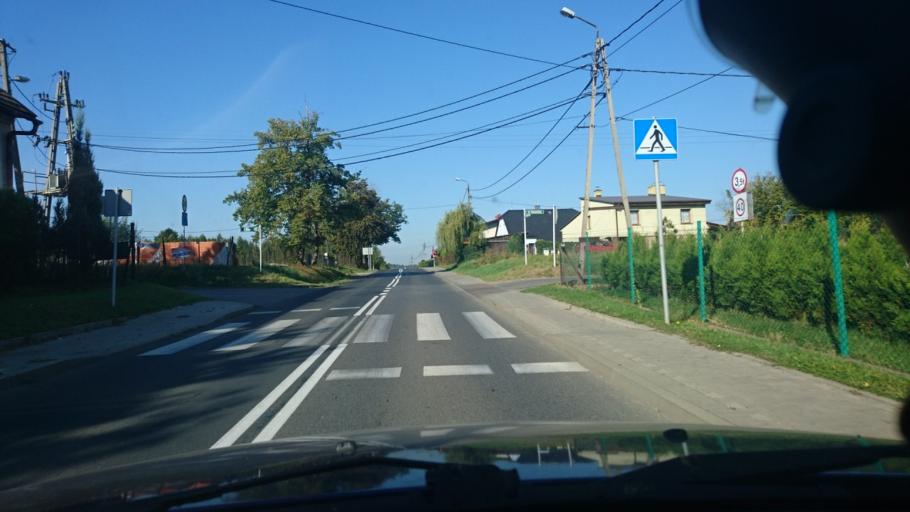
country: PL
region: Silesian Voivodeship
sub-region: Bielsko-Biala
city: Bielsko-Biala
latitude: 49.8507
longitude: 19.0573
